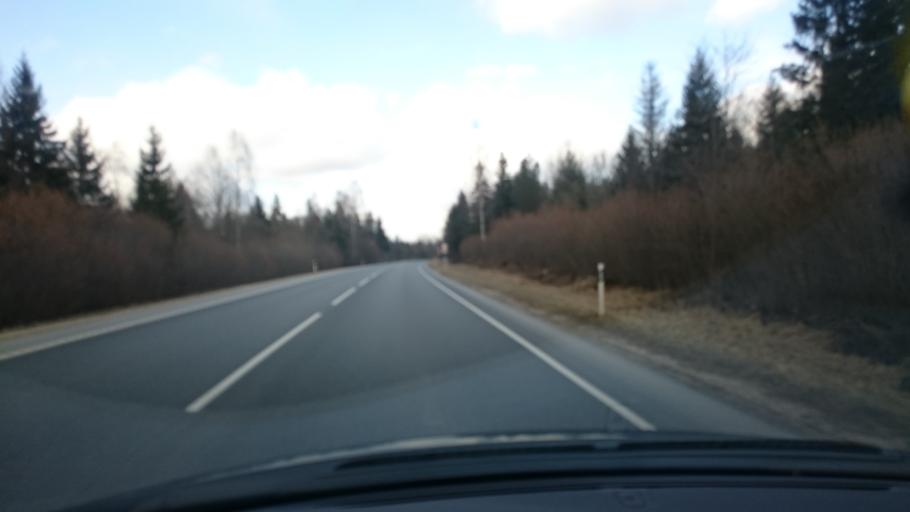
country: EE
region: Harju
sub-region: Nissi vald
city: Turba
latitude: 59.1105
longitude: 24.2575
